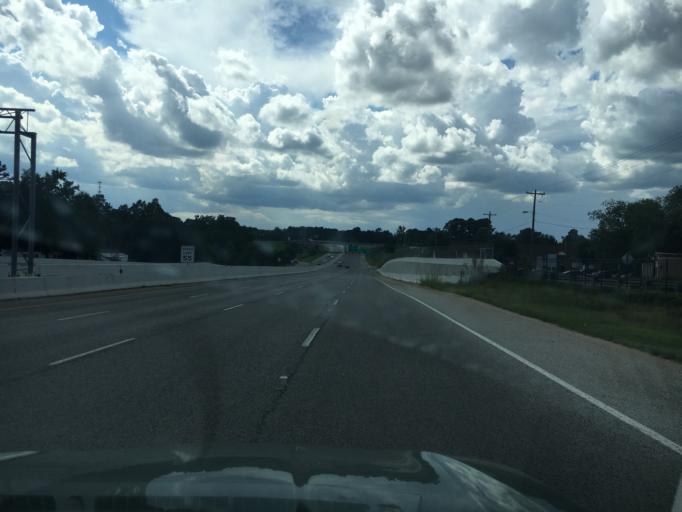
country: US
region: South Carolina
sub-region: Spartanburg County
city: Valley Falls
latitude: 34.9945
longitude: -81.9727
